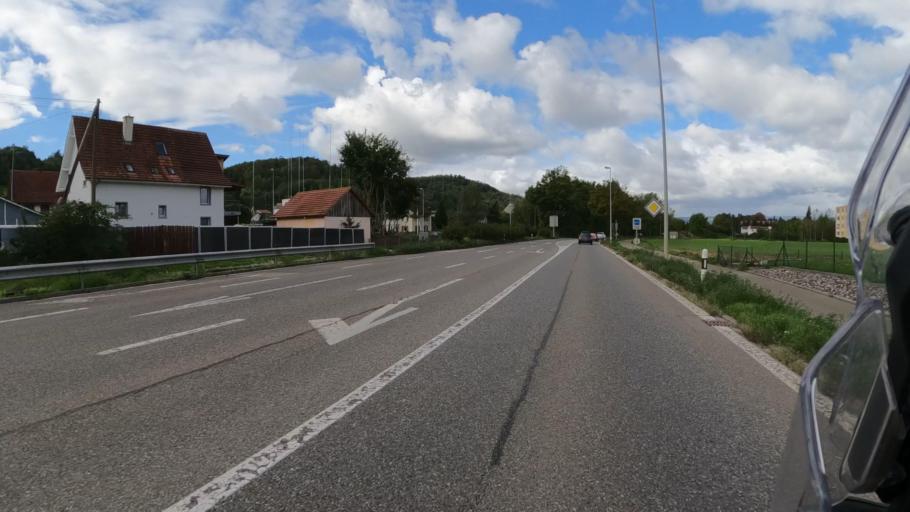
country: CH
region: Aargau
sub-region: Bezirk Zurzach
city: Bad Zurzach
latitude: 47.5721
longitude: 8.3206
